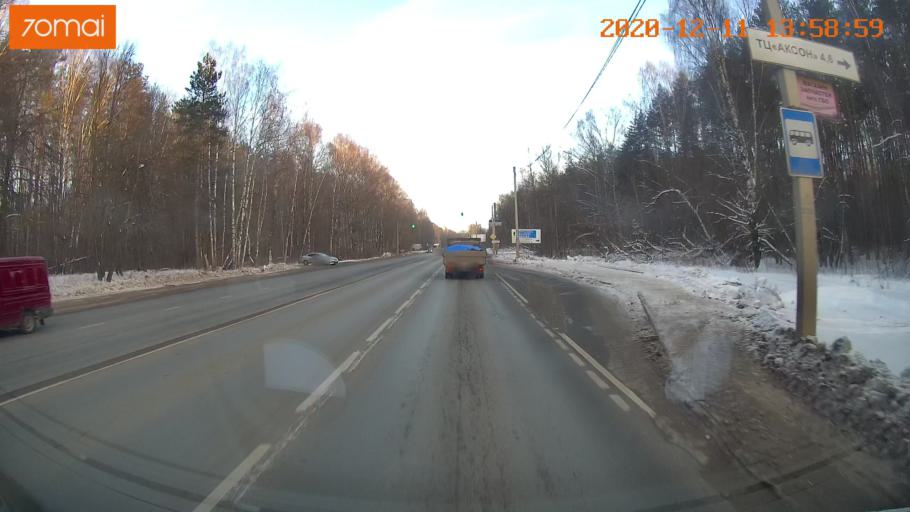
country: RU
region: Kostroma
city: Oktyabr'skiy
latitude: 57.7824
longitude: 41.0030
